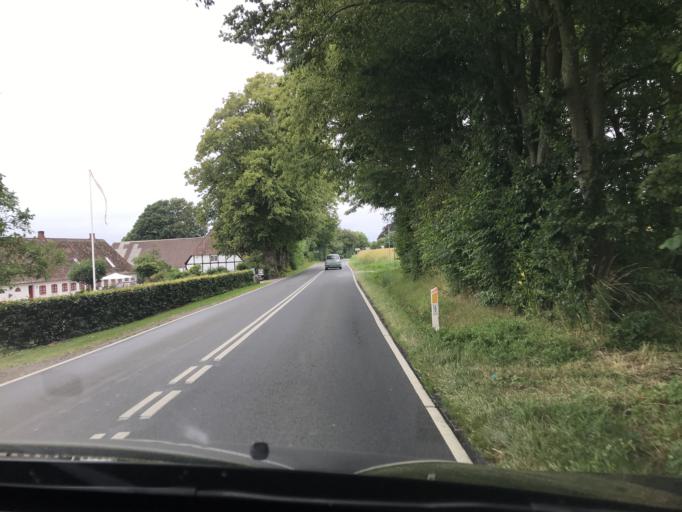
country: DK
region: South Denmark
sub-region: AEro Kommune
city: AEroskobing
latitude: 54.8676
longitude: 10.3647
